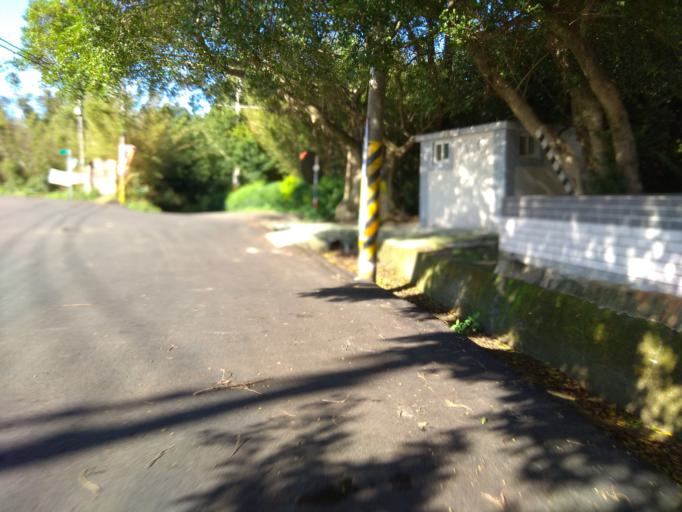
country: TW
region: Taiwan
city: Daxi
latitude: 24.8646
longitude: 121.1548
